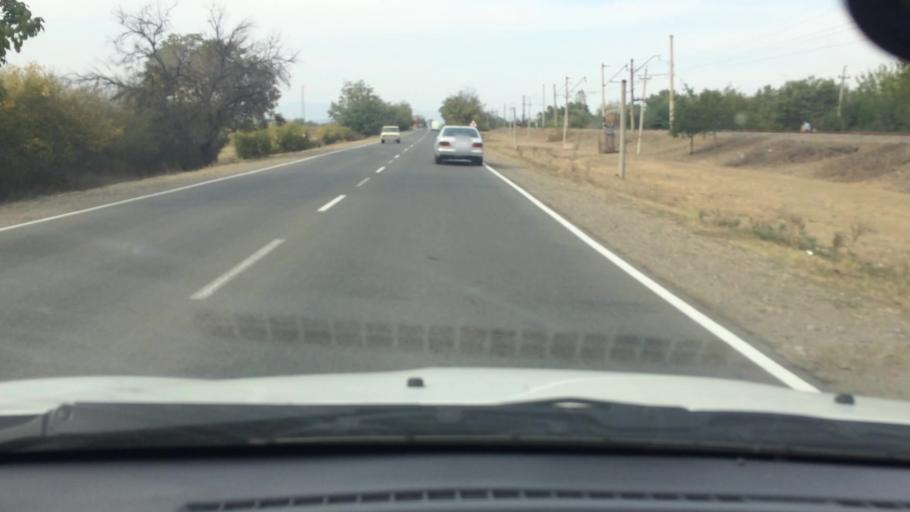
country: GE
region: Kvemo Kartli
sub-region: Marneuli
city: Marneuli
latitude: 41.4266
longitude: 44.8228
